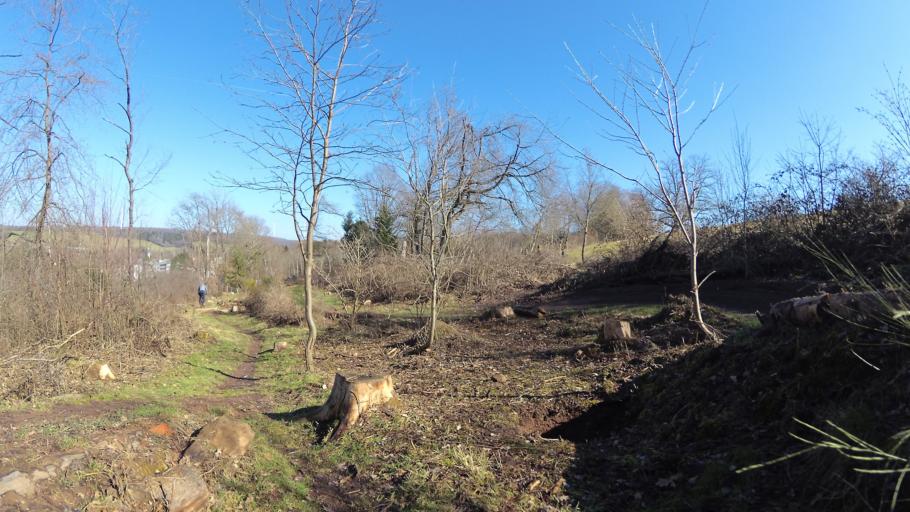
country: DE
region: Saarland
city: Ottweiler
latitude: 49.4095
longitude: 7.1933
